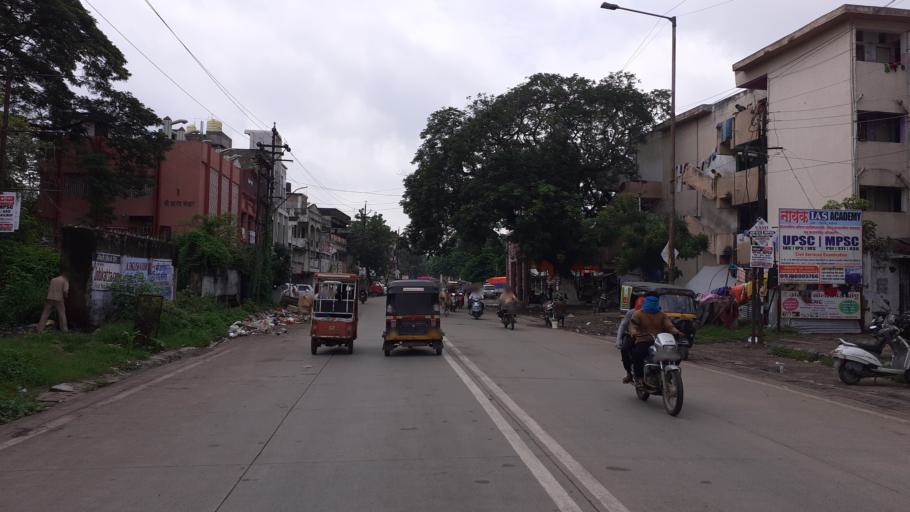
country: IN
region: Maharashtra
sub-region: Nagpur Division
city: Nagpur
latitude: 21.1255
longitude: 79.1131
